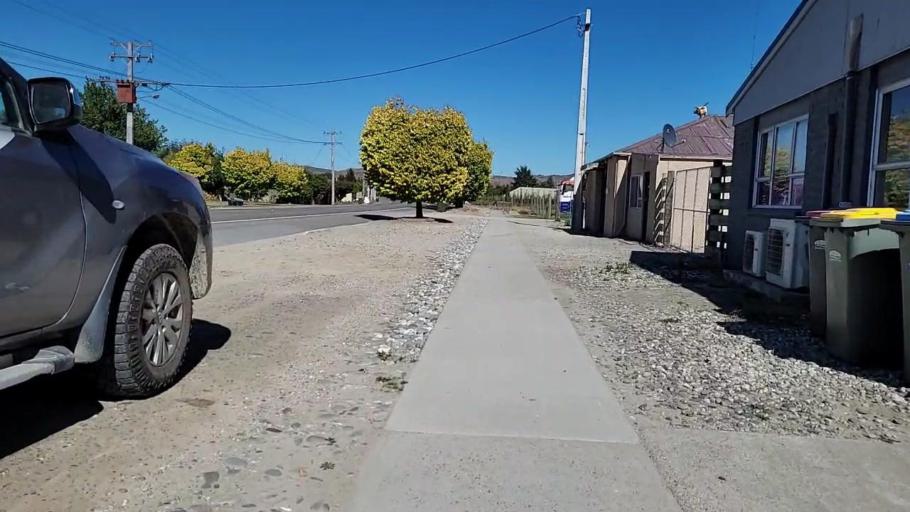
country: NZ
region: Otago
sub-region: Queenstown-Lakes District
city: Wanaka
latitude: -45.0974
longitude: 169.5985
